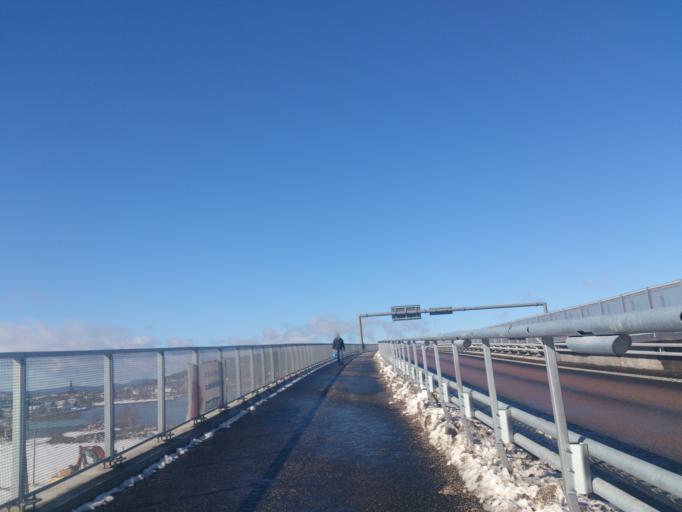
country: SE
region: Vaesternorrland
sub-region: Sundsvalls Kommun
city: Sundsvall
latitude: 62.3826
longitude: 17.3500
